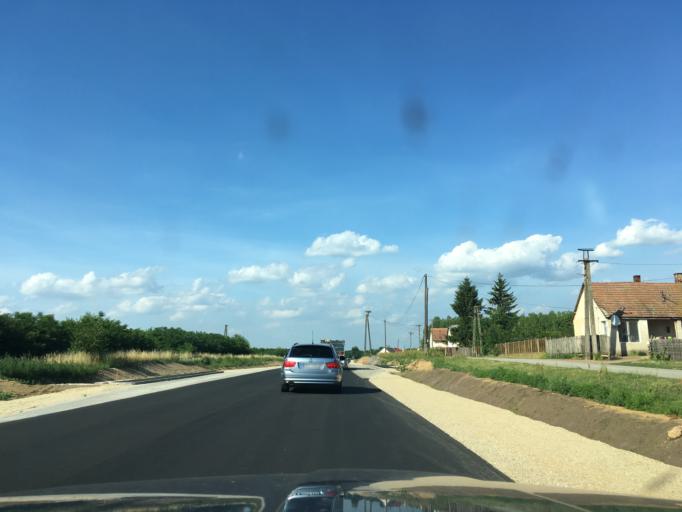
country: HU
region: Hajdu-Bihar
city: Hajdusamson
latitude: 47.6374
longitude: 21.8051
